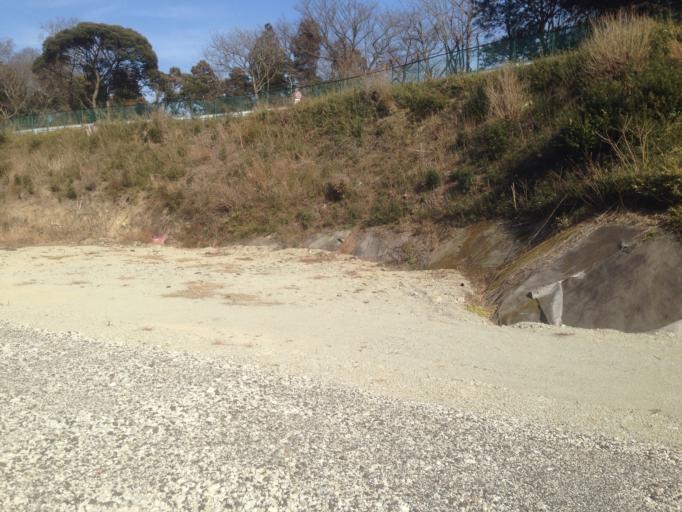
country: JP
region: Kanagawa
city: Yokosuka
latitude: 35.2456
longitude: 139.6444
